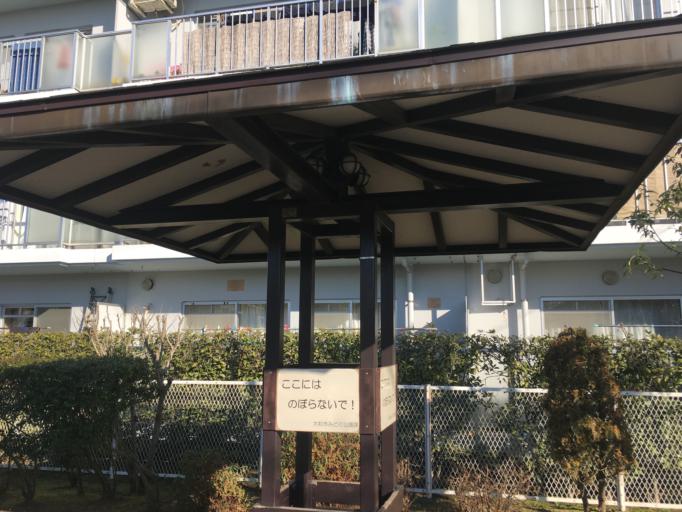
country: JP
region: Kanagawa
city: Minami-rinkan
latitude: 35.4605
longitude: 139.4691
